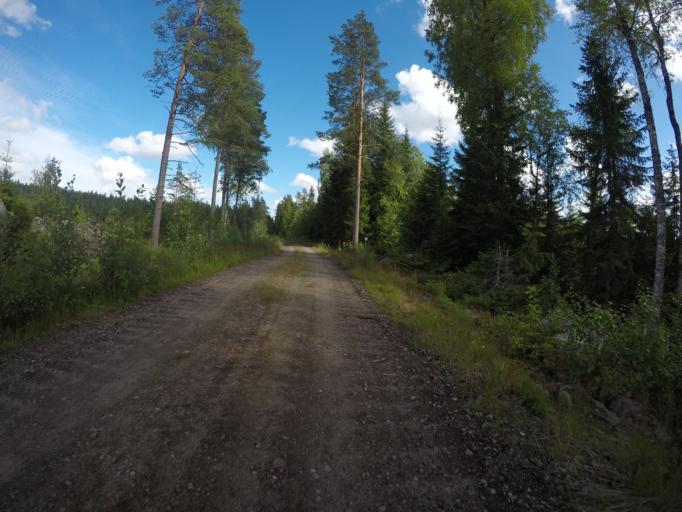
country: SE
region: Dalarna
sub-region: Ludvika Kommun
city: Abborrberget
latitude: 60.0282
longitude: 14.6128
